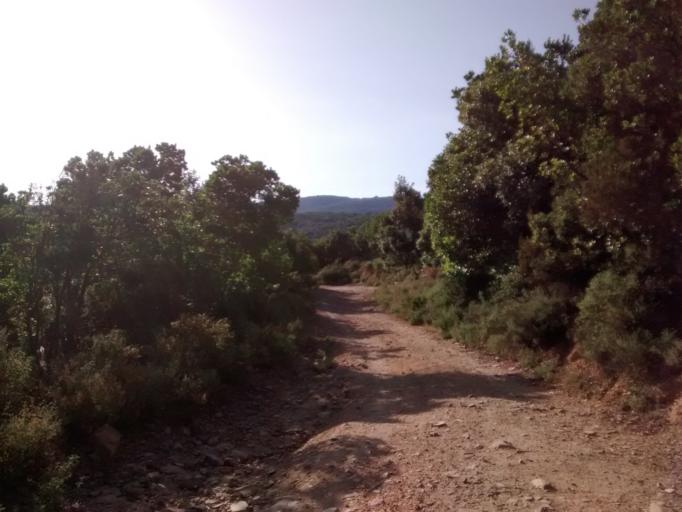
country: IT
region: Sardinia
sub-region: Provincia di Cagliari
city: Castiadas
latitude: 39.2277
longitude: 9.4680
